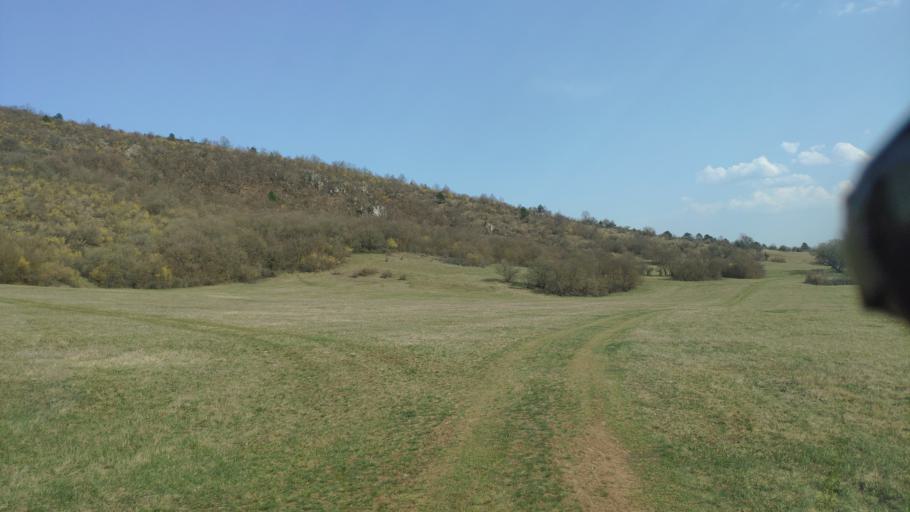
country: SK
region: Kosicky
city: Medzev
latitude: 48.6234
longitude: 20.9026
